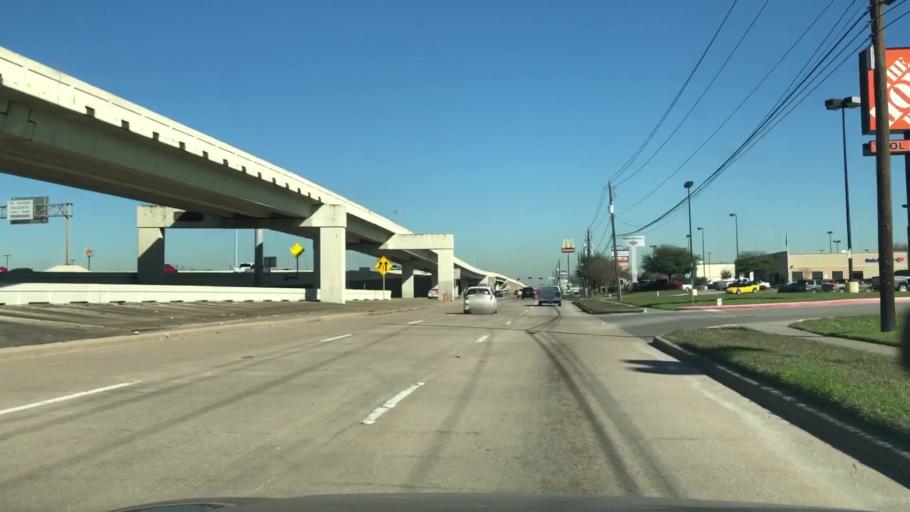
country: US
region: Texas
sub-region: Harris County
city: Aldine
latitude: 29.8674
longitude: -95.3311
